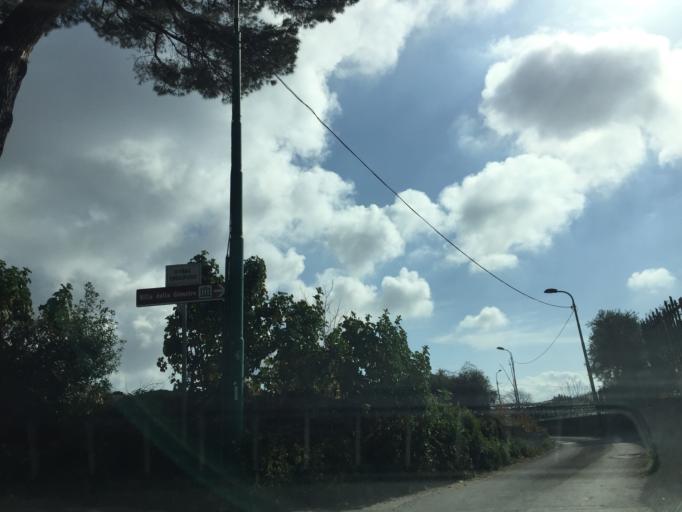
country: IT
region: Campania
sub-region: Provincia di Napoli
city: Torre del Greco
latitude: 40.7795
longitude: 14.4136
